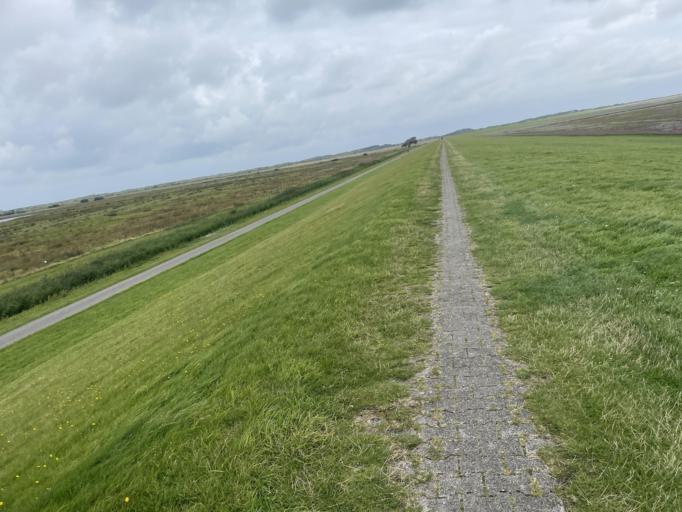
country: DE
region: Lower Saxony
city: Borkum
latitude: 53.5896
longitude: 6.7365
